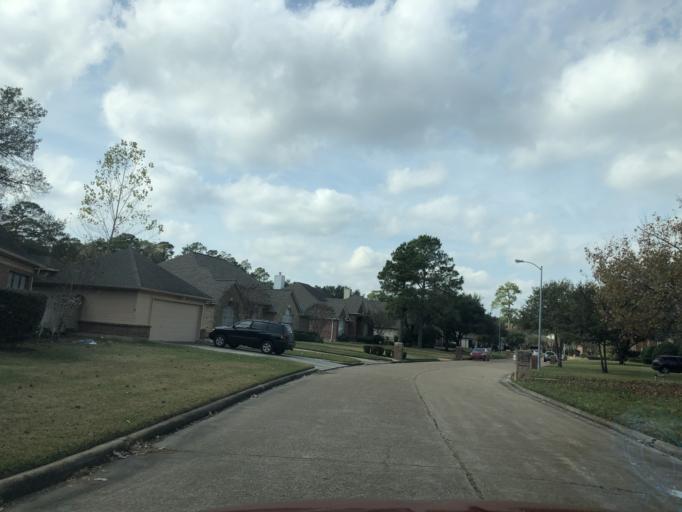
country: US
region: Texas
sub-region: Harris County
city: Tomball
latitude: 30.0308
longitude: -95.5379
